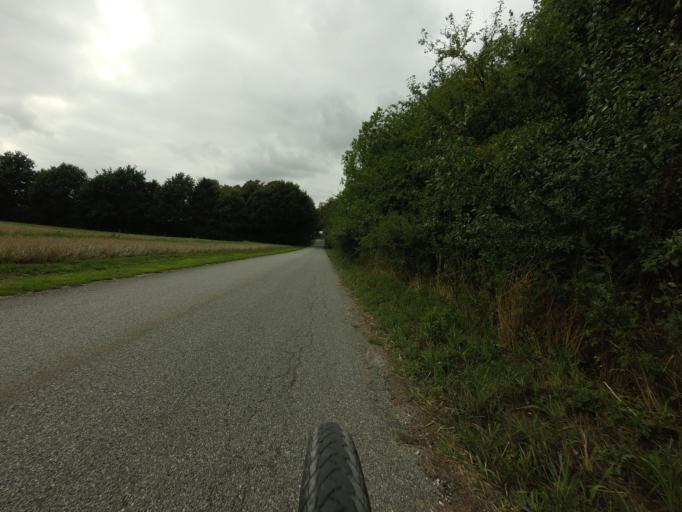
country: DK
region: Zealand
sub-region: Stevns Kommune
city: Store Heddinge
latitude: 55.3392
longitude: 12.4256
